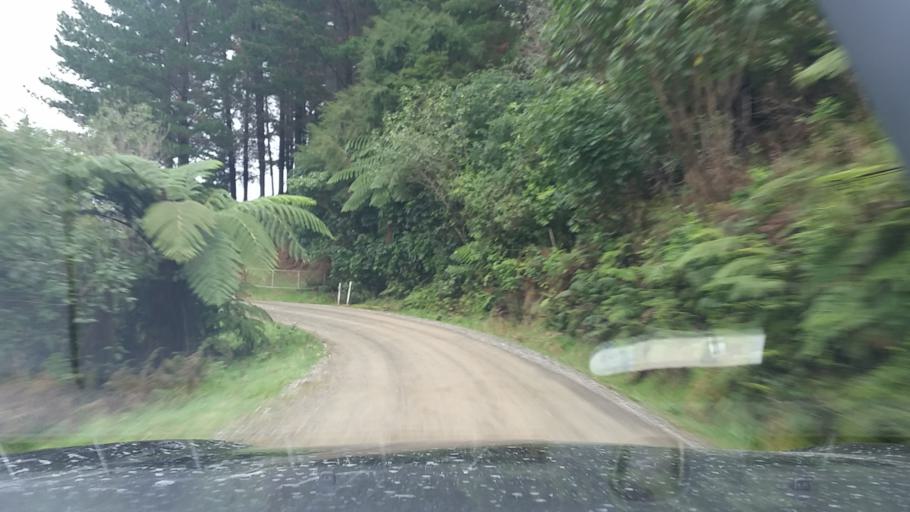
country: NZ
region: Marlborough
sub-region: Marlborough District
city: Picton
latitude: -41.1786
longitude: 173.9915
